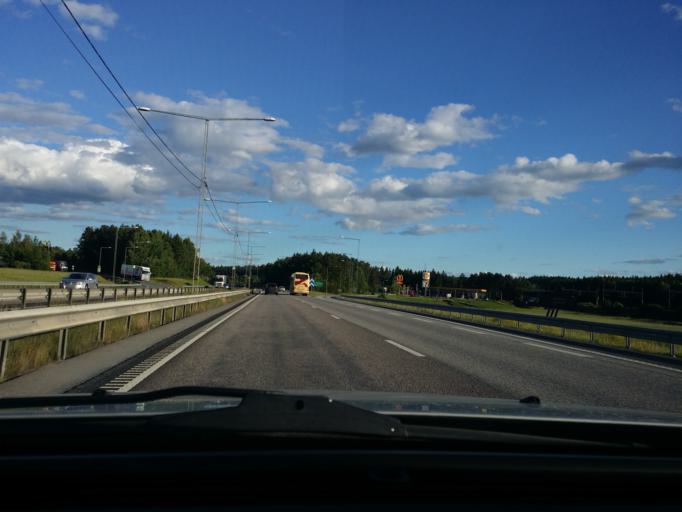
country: SE
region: Stockholm
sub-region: Sigtuna Kommun
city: Rosersberg
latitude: 59.5537
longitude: 17.8986
